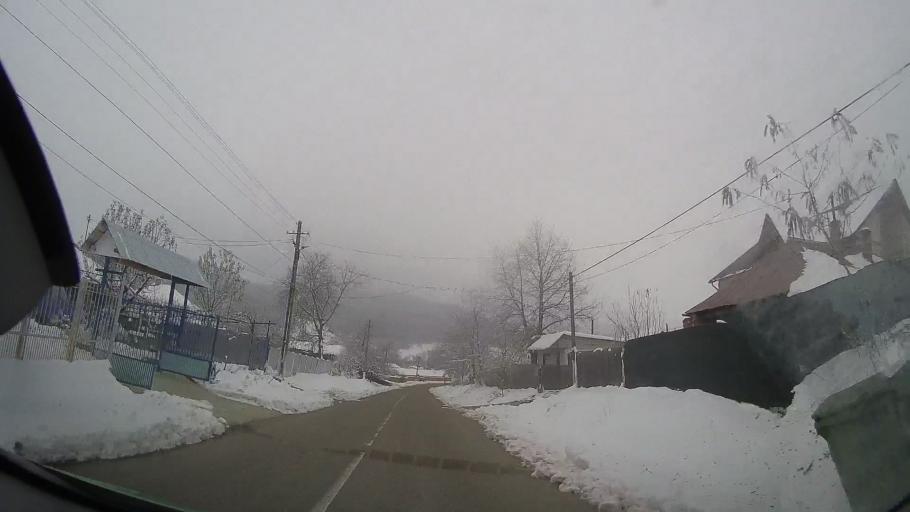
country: RO
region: Neamt
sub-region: Comuna Bozieni
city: Bozieni
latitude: 46.8373
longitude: 27.1661
